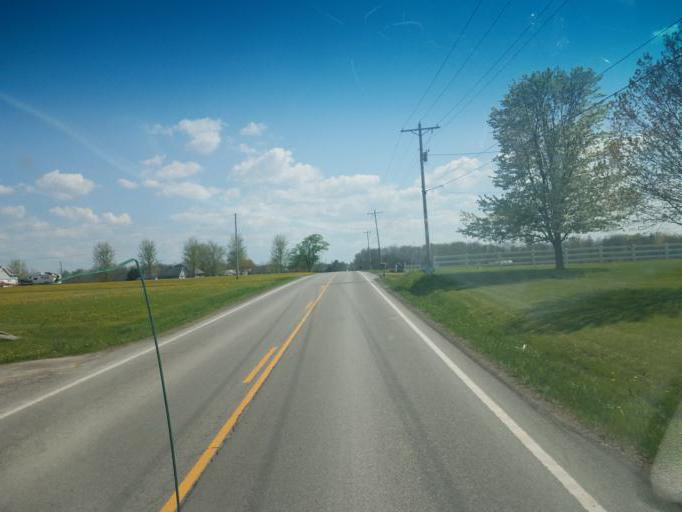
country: US
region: Ohio
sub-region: Wayne County
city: West Salem
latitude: 40.9277
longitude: -82.1091
